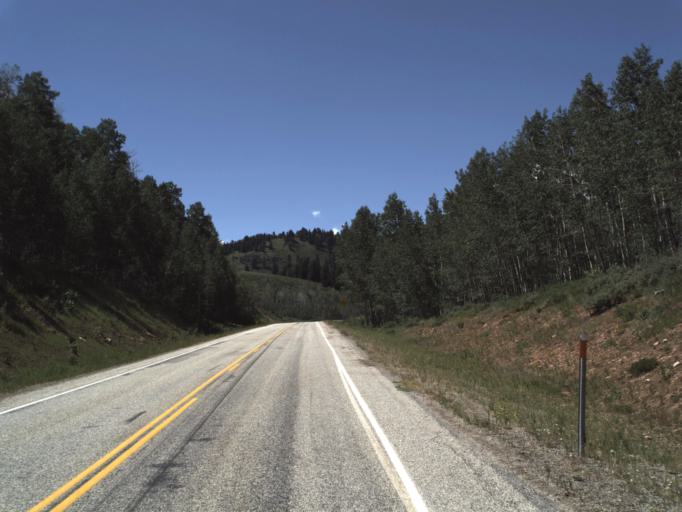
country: US
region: Utah
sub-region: Rich County
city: Randolph
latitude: 41.4728
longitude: -111.4485
